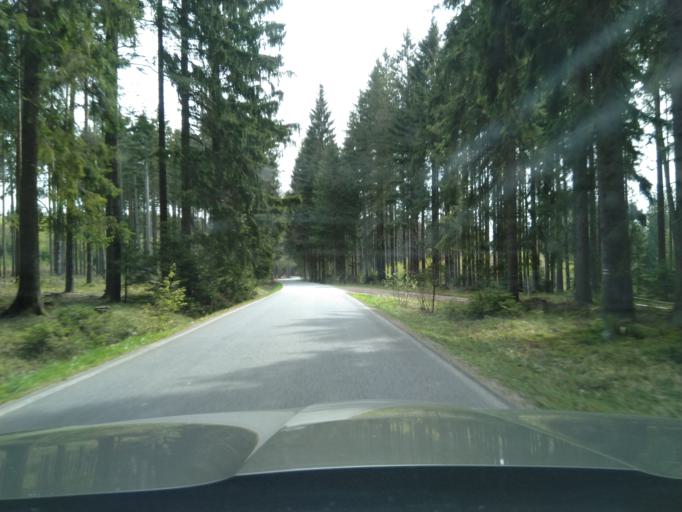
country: CZ
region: Jihocesky
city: Vacov
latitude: 49.1527
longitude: 13.6972
